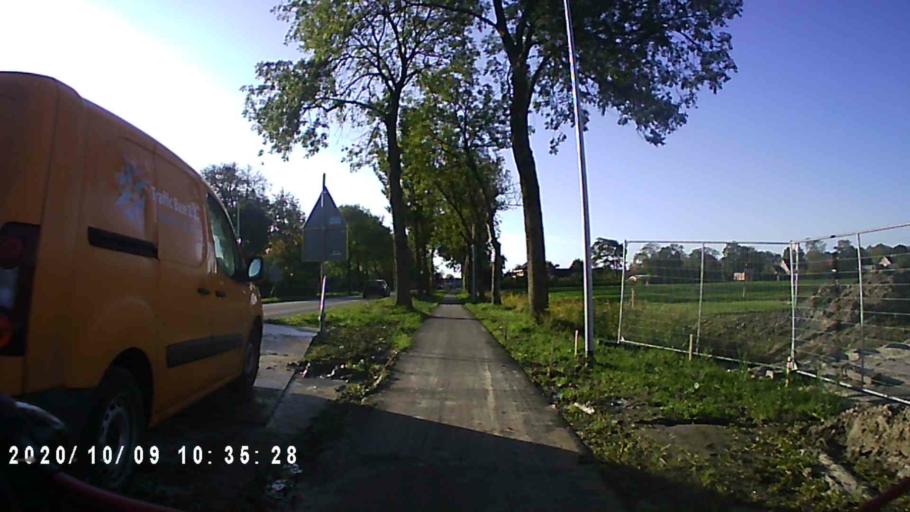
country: NL
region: Groningen
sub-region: Gemeente Winsum
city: Winsum
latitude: 53.2980
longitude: 6.5337
